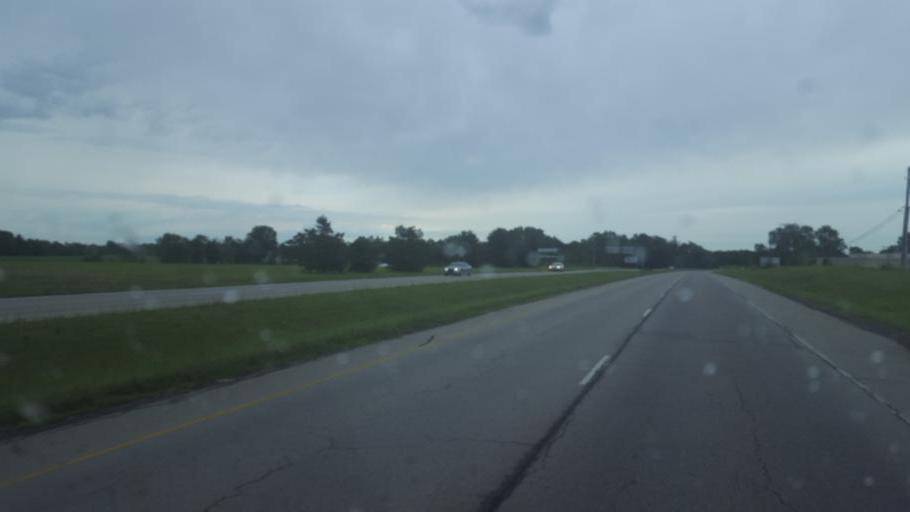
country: US
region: Ohio
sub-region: Richland County
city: Ontario
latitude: 40.7715
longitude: -82.5801
